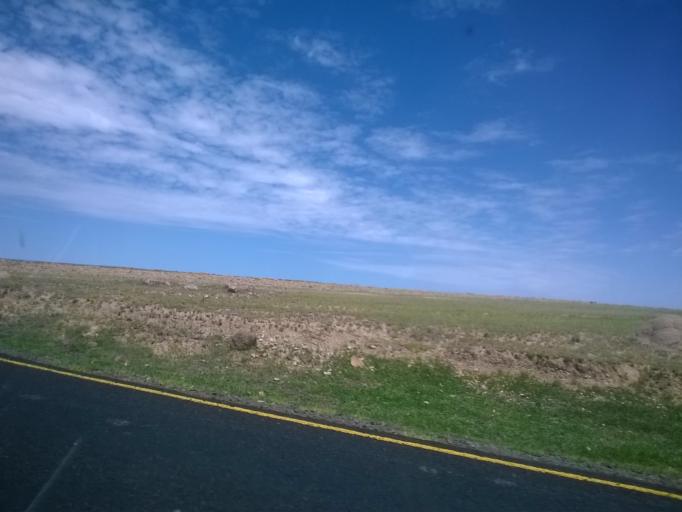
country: LS
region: Berea
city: Teyateyaneng
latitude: -29.0909
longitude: 27.8577
